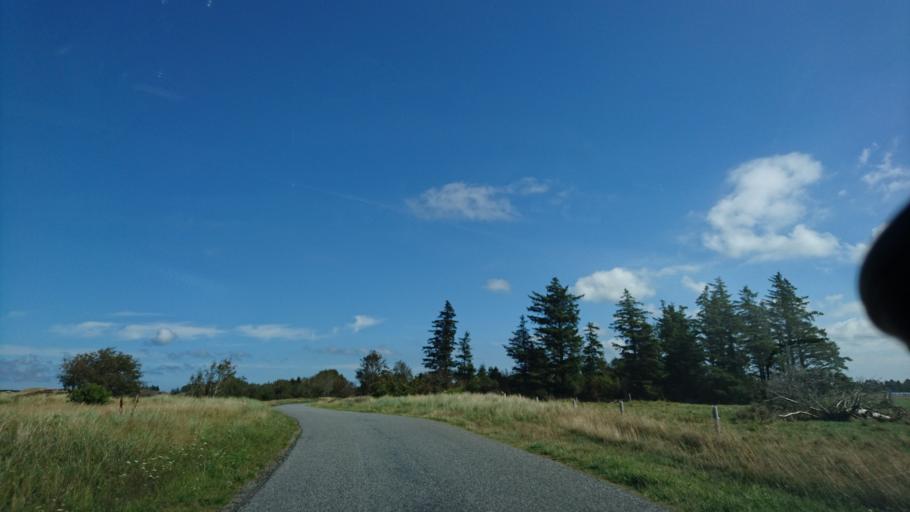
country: DK
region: North Denmark
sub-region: Frederikshavn Kommune
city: Strandby
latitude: 57.6252
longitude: 10.3812
